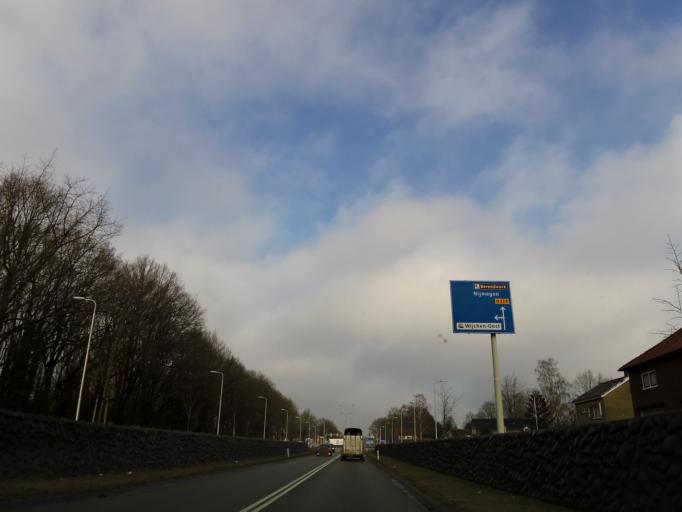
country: NL
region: Gelderland
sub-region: Gemeente Wijchen
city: Wijchen
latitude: 51.8076
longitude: 5.7583
